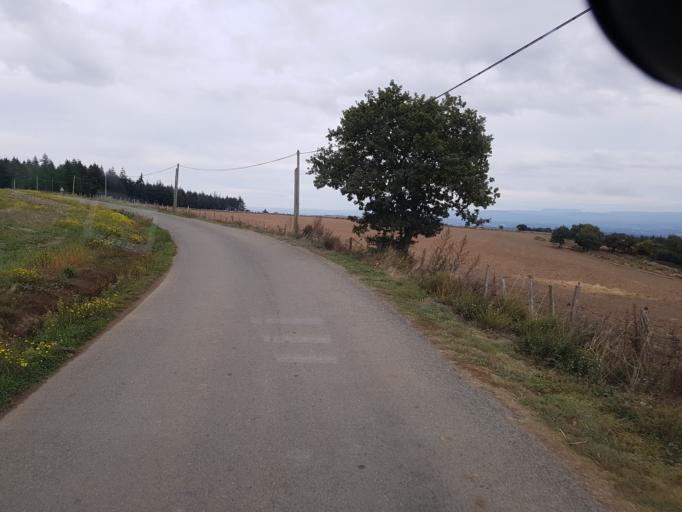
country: FR
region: Languedoc-Roussillon
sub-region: Departement de l'Aude
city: Cuxac-Cabardes
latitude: 43.3640
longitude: 2.3086
